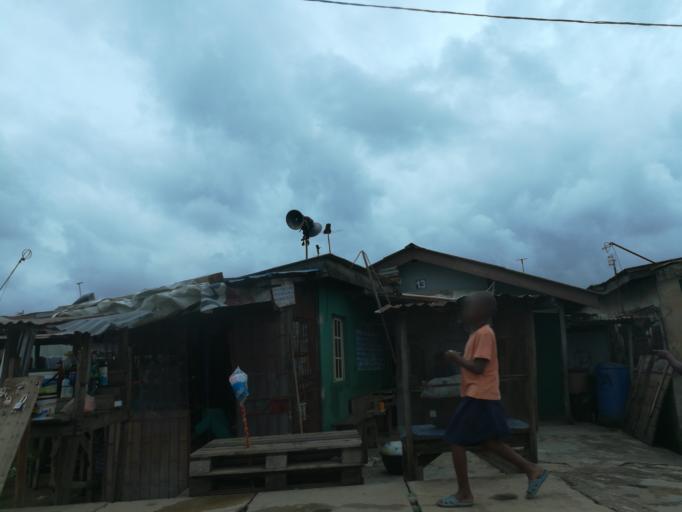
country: NG
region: Lagos
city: Agege
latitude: 6.6150
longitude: 3.3093
